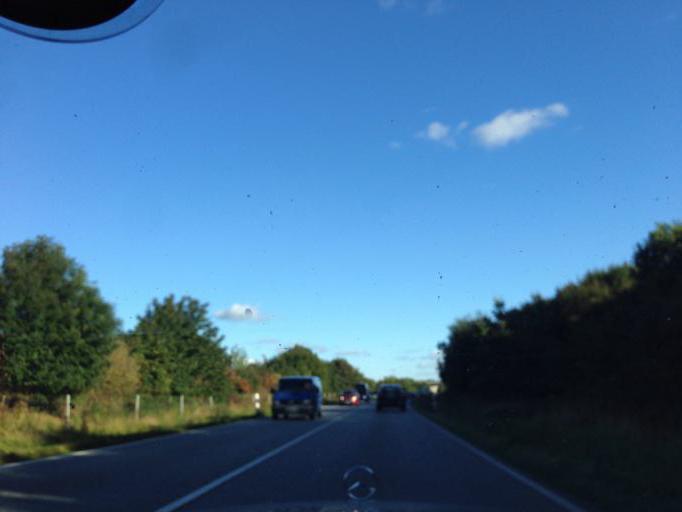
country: DE
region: Schleswig-Holstein
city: Latendorf
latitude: 54.0248
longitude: 10.0583
